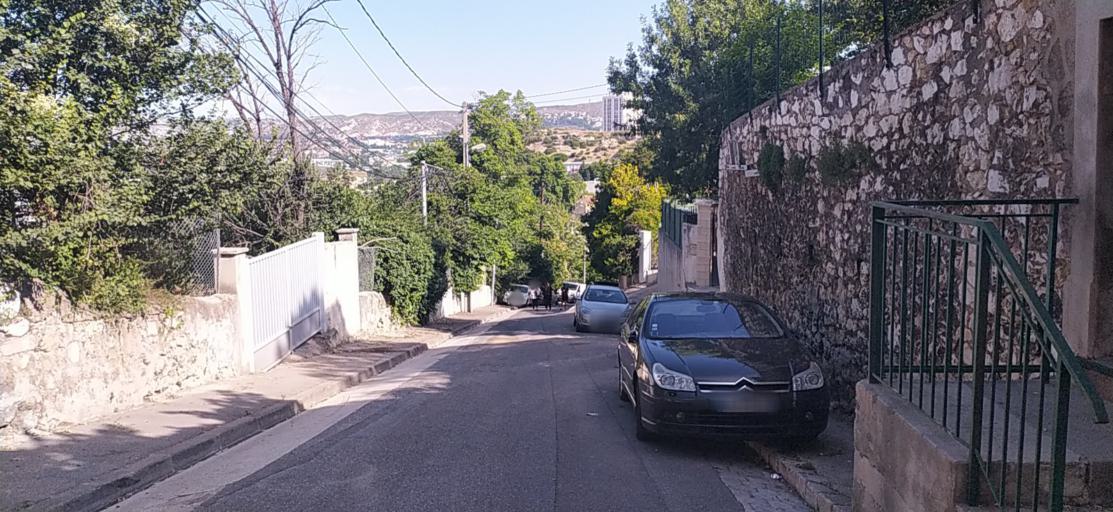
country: FR
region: Provence-Alpes-Cote d'Azur
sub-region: Departement des Bouches-du-Rhone
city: Marseille 16
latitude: 43.3414
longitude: 5.3506
